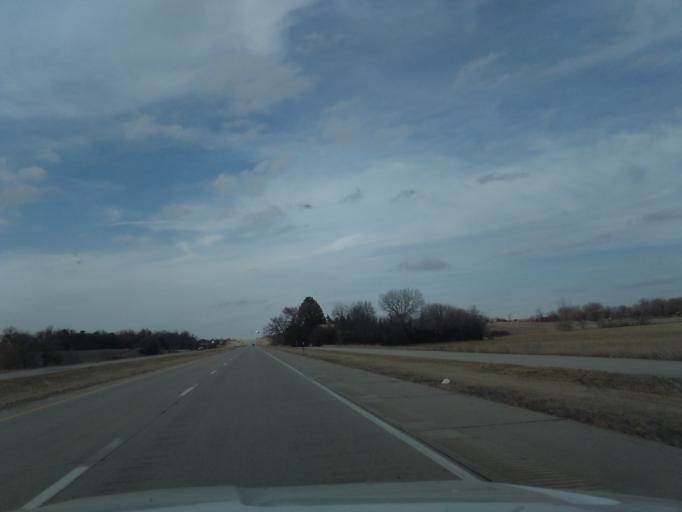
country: US
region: Nebraska
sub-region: Lancaster County
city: Hickman
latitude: 40.4805
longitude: -96.7043
